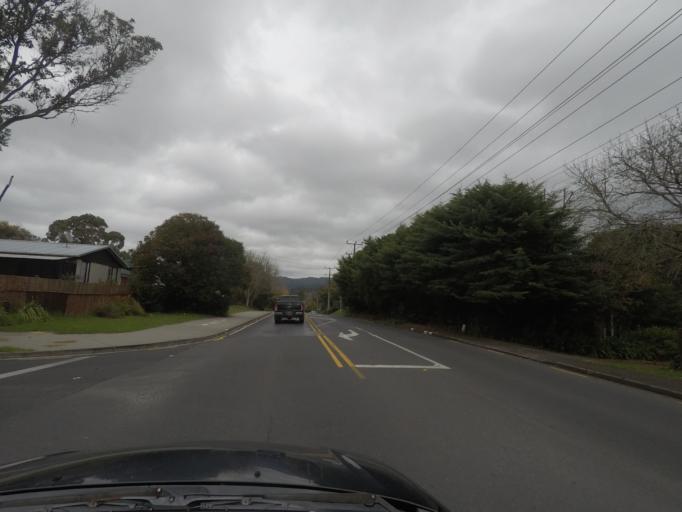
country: NZ
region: Auckland
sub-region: Auckland
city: Waitakere
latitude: -36.9086
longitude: 174.6271
